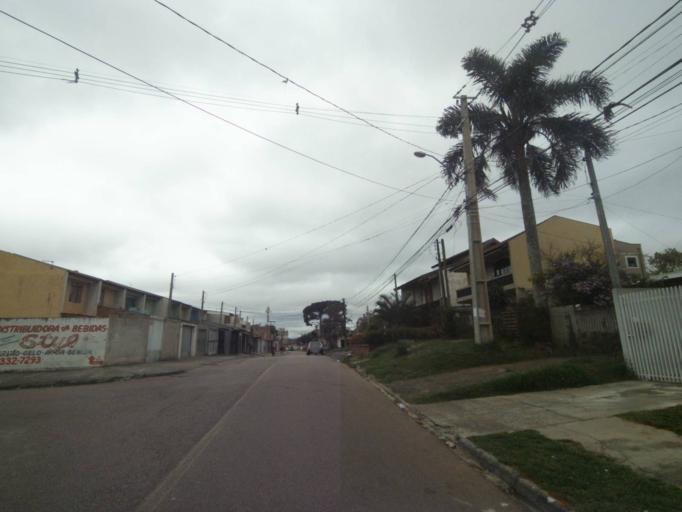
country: BR
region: Parana
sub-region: Curitiba
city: Curitiba
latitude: -25.4725
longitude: -49.2736
